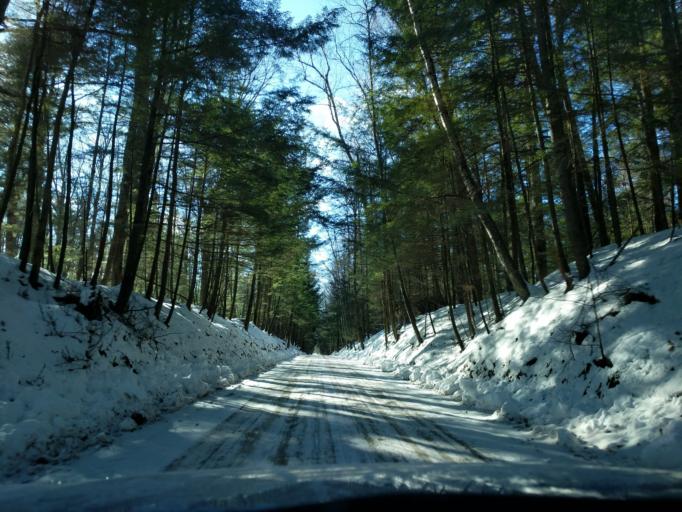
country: US
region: Wisconsin
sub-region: Menominee County
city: Keshena
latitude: 45.0931
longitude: -88.6189
